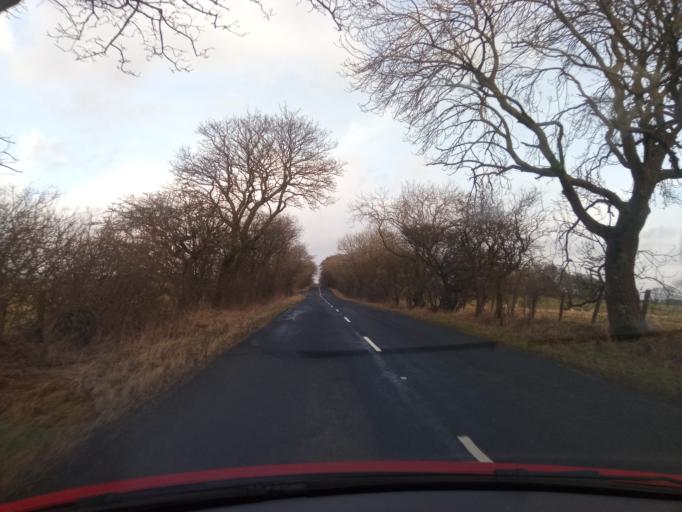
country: GB
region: England
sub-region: Northumberland
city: Acomb
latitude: 55.0928
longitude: -2.0542
